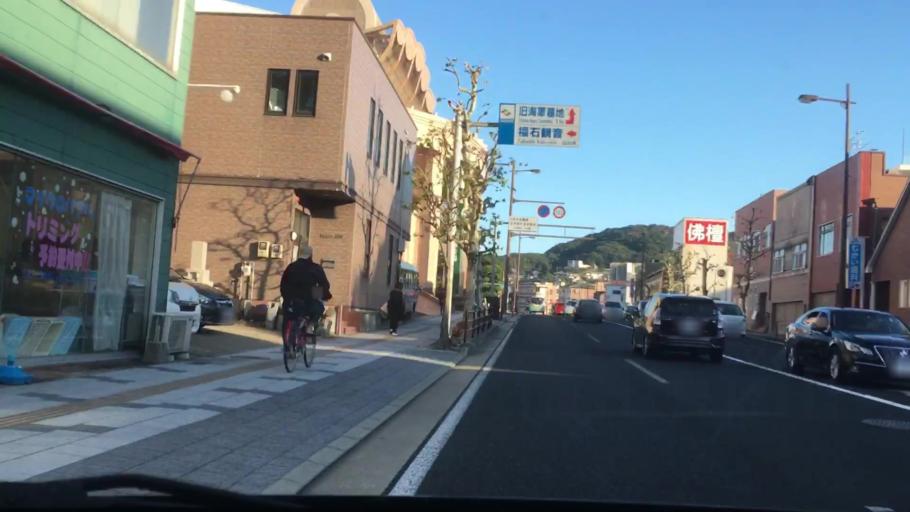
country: JP
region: Nagasaki
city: Sasebo
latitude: 33.1603
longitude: 129.7321
